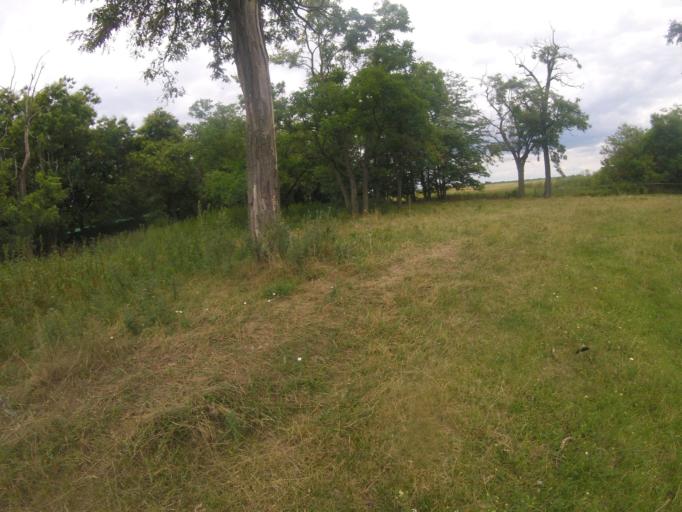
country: HU
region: Hajdu-Bihar
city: Egyek
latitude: 47.5736
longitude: 20.9430
